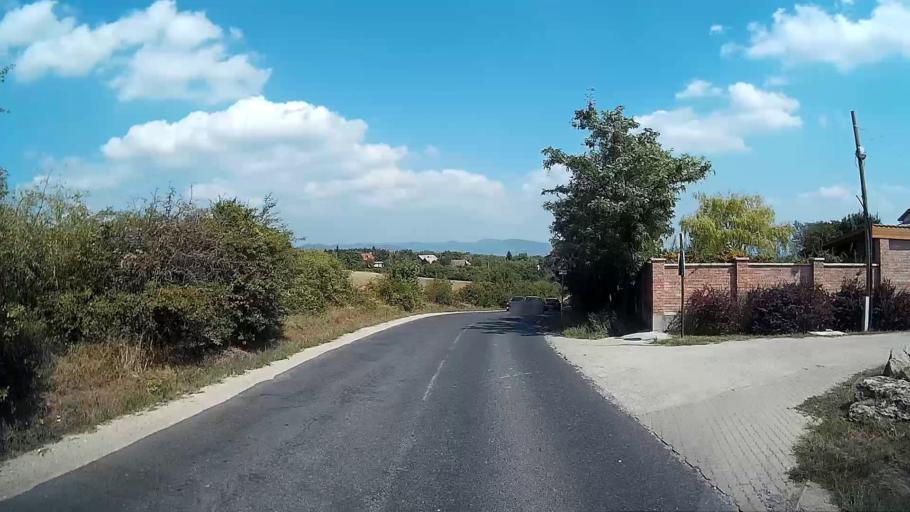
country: HU
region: Pest
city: Urom
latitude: 47.6089
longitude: 19.0210
